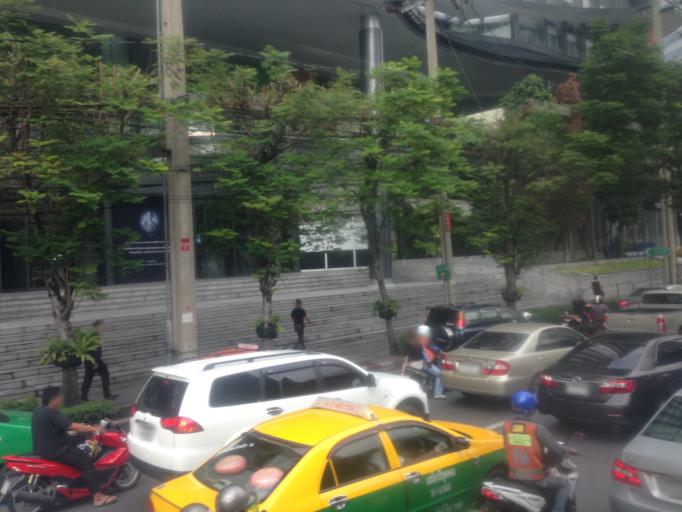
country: TH
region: Bangkok
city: Bang Rak
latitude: 13.7208
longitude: 100.5306
